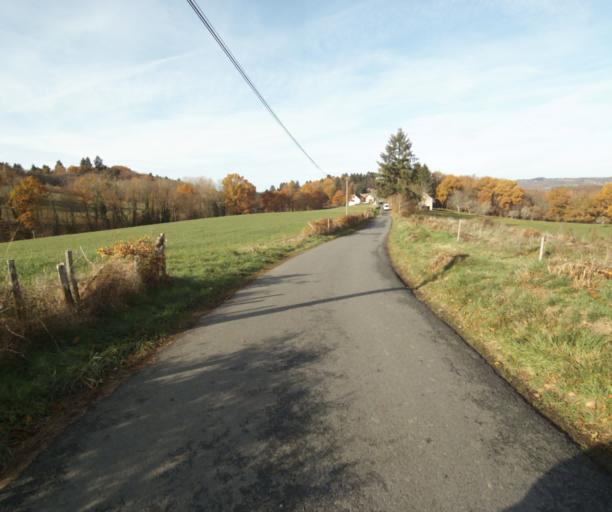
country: FR
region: Limousin
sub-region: Departement de la Correze
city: Sainte-Fortunade
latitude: 45.2125
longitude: 1.7581
